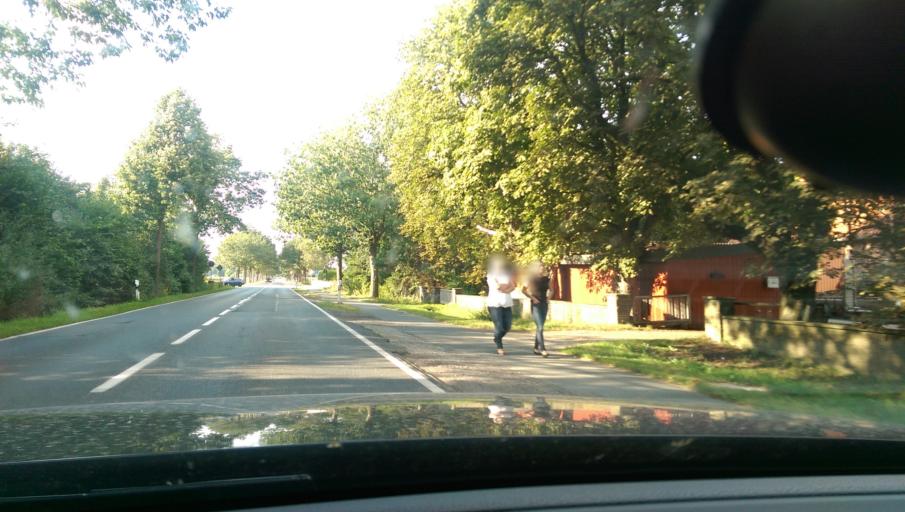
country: DE
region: Lower Saxony
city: Neustadt am Rubenberge
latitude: 52.5165
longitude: 9.4517
